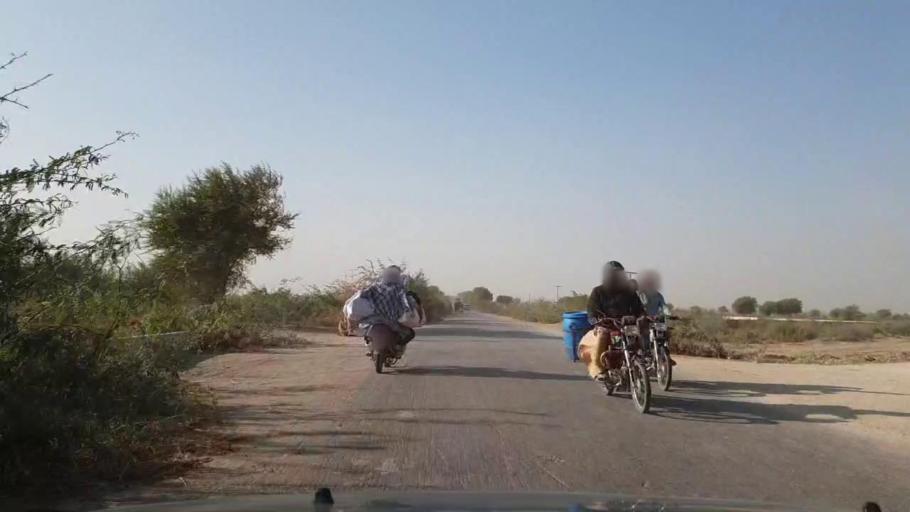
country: PK
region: Sindh
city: Tando Ghulam Ali
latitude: 25.1512
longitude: 68.8592
